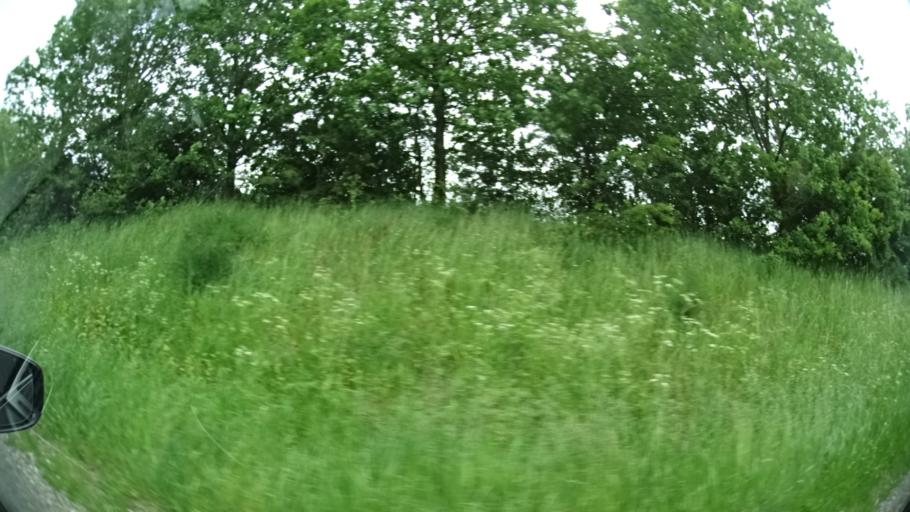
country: DK
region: Central Jutland
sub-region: Norddjurs Kommune
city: Grenaa
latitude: 56.4591
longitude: 10.7127
